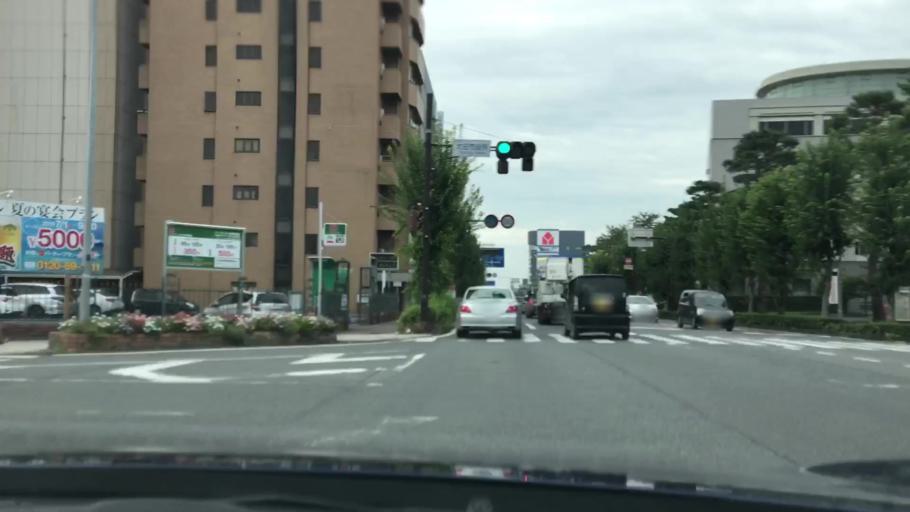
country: JP
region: Gunma
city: Ota
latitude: 36.2919
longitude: 139.3765
